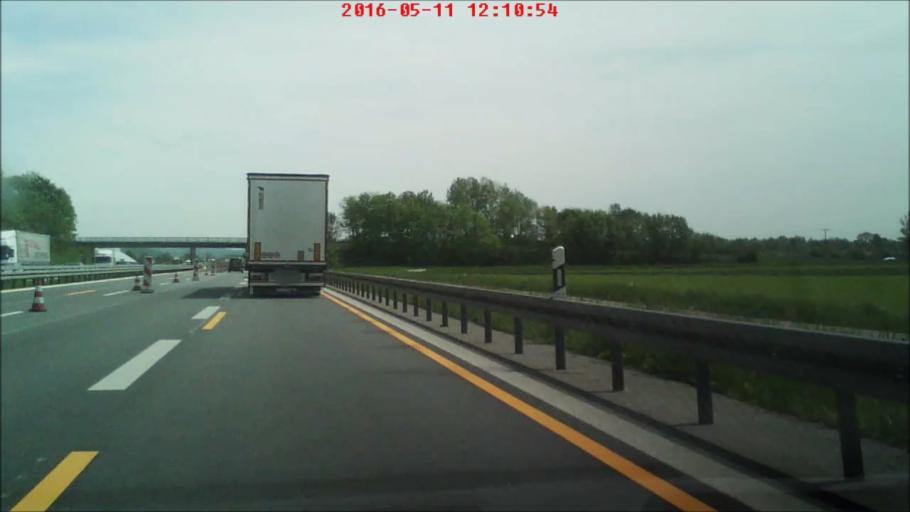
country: DE
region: Bavaria
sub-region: Lower Bavaria
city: Offenberg
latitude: 48.8591
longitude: 12.8585
